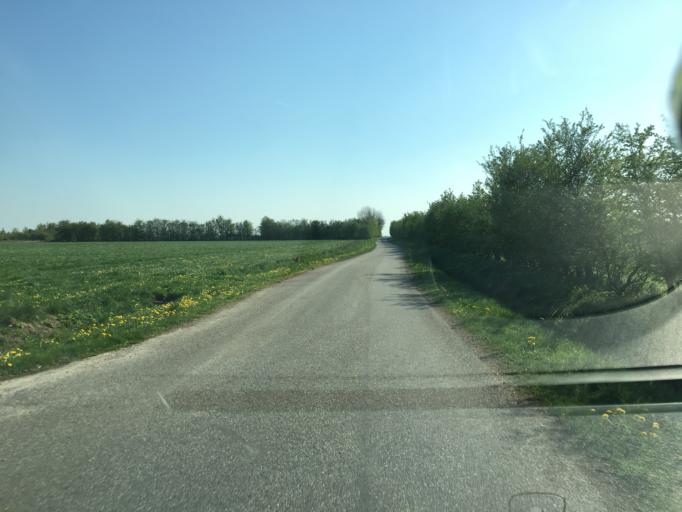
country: DK
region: South Denmark
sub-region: Tonder Kommune
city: Toftlund
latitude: 55.1840
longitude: 9.1102
